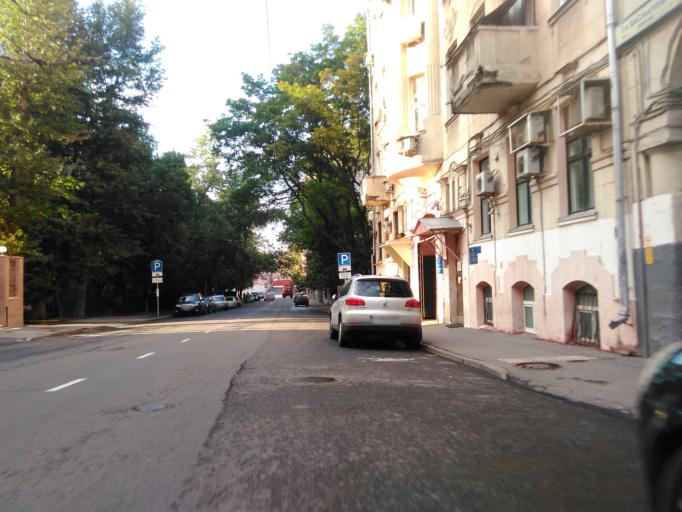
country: RU
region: Moscow
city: Sokol'niki
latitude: 55.7707
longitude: 37.6634
